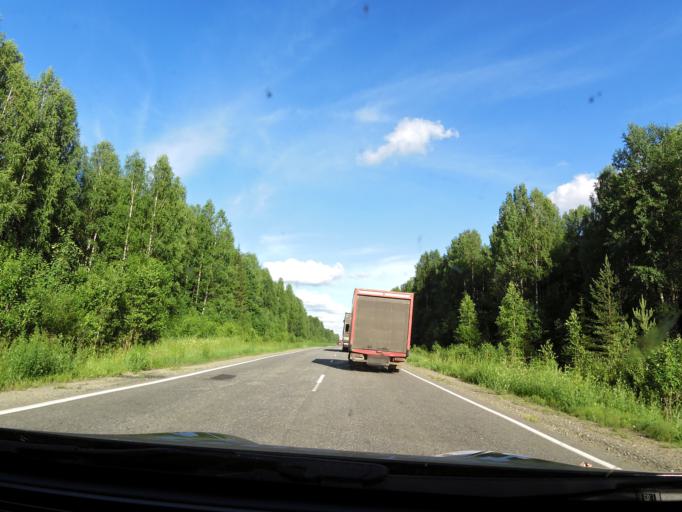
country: RU
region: Kirov
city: Omutninsk
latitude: 58.7671
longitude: 51.9751
